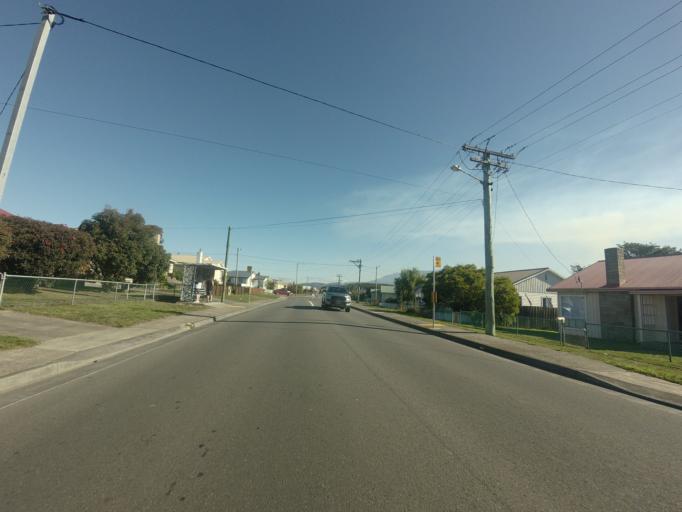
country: AU
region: Tasmania
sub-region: Clarence
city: Warrane
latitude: -42.8618
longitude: 147.3745
